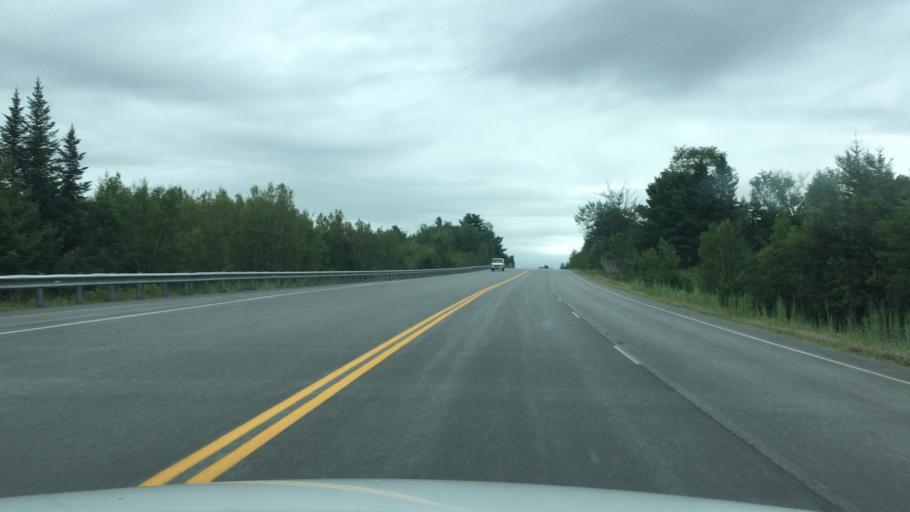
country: US
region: Maine
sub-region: Hancock County
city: Franklin
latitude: 44.8468
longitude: -68.3381
